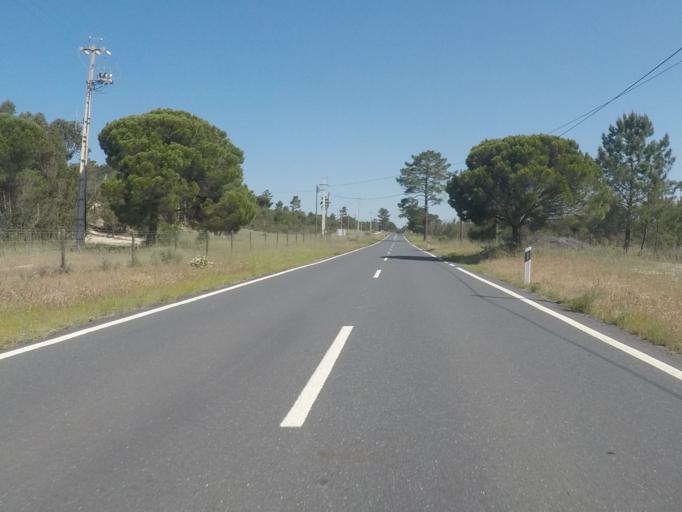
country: PT
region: Setubal
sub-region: Grandola
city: Grandola
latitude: 38.2331
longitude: -8.7359
